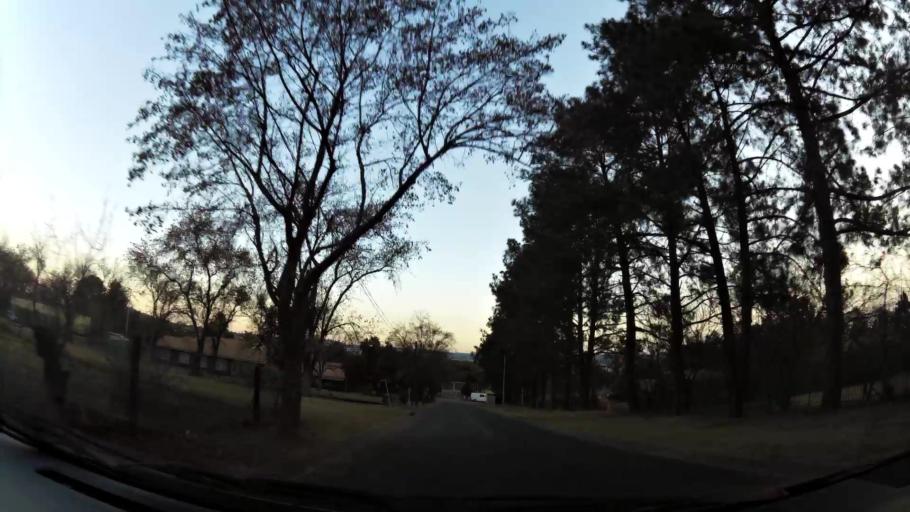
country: ZA
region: Gauteng
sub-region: City of Johannesburg Metropolitan Municipality
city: Diepsloot
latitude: -26.0063
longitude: 28.0438
